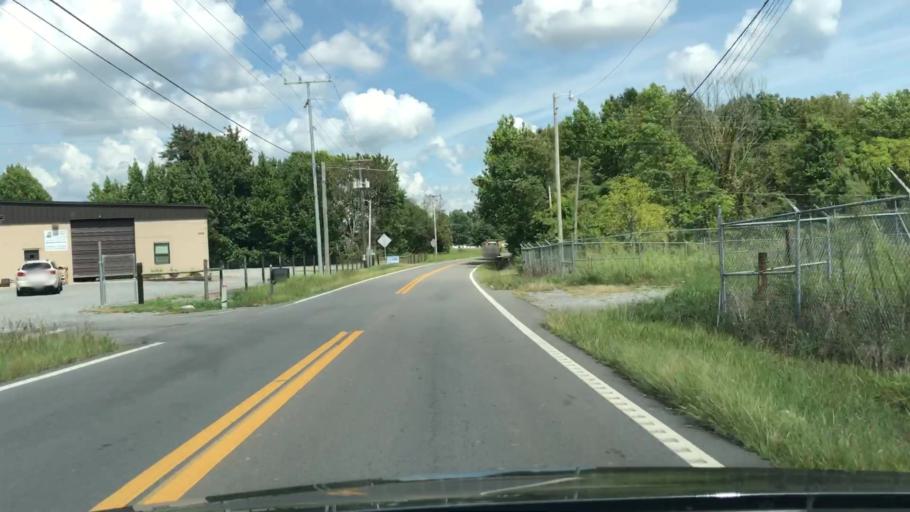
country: US
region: Tennessee
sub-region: Sumner County
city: White House
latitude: 36.5112
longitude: -86.5739
